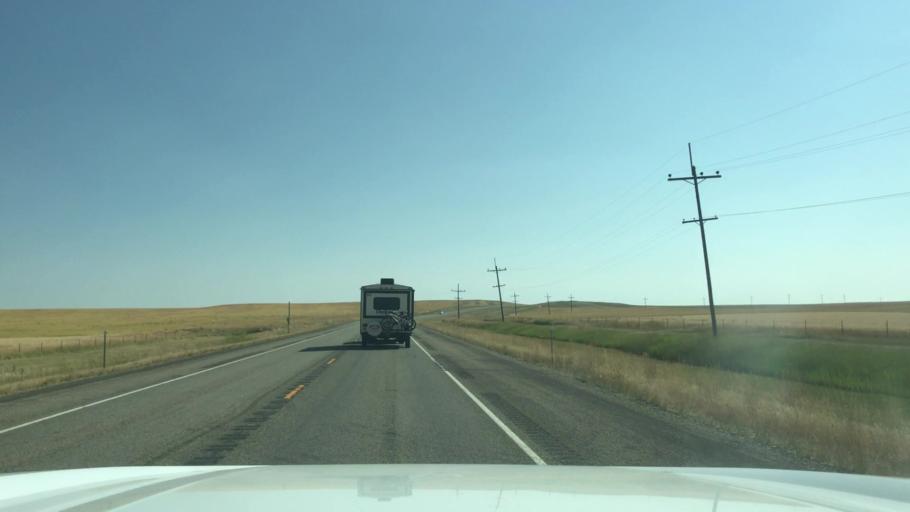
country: US
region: Montana
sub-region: Wheatland County
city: Harlowton
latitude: 46.4764
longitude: -109.7661
